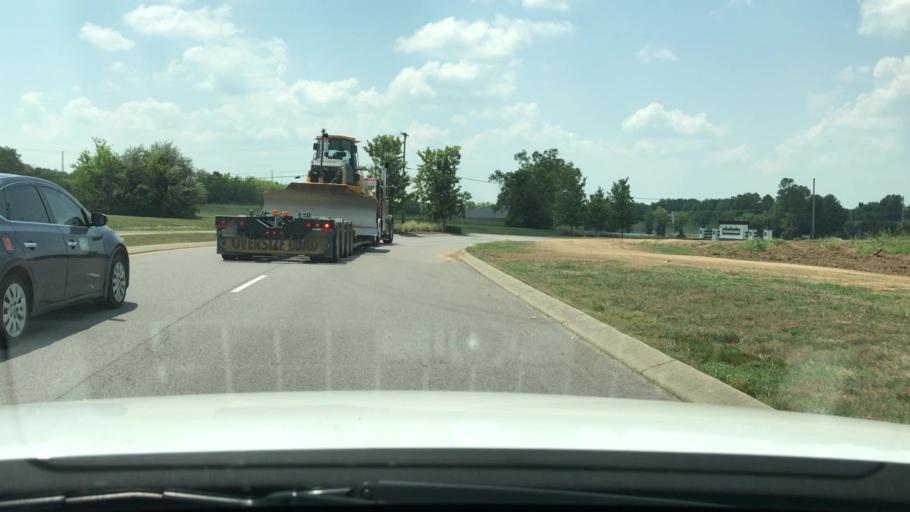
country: US
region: Tennessee
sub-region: Sumner County
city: Gallatin
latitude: 36.3627
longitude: -86.4464
